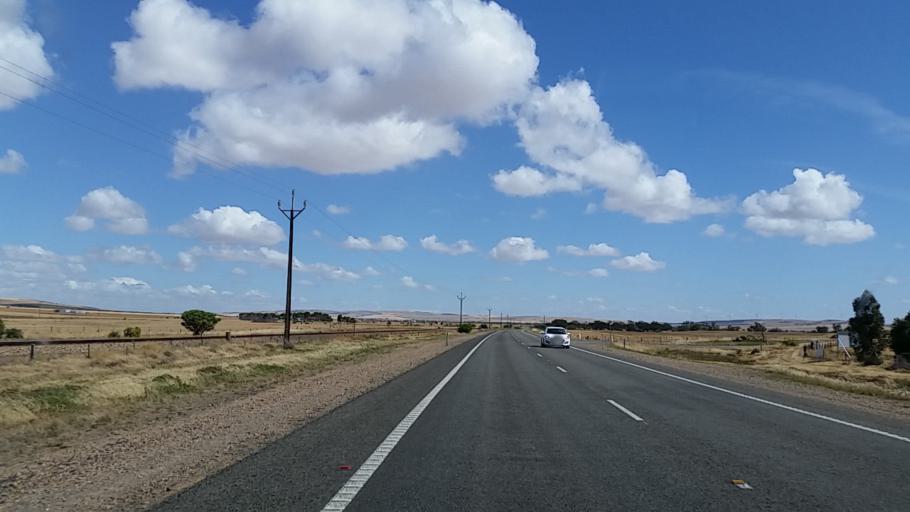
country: AU
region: South Australia
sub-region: Port Pirie City and Dists
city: Crystal Brook
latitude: -33.3948
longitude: 138.1695
